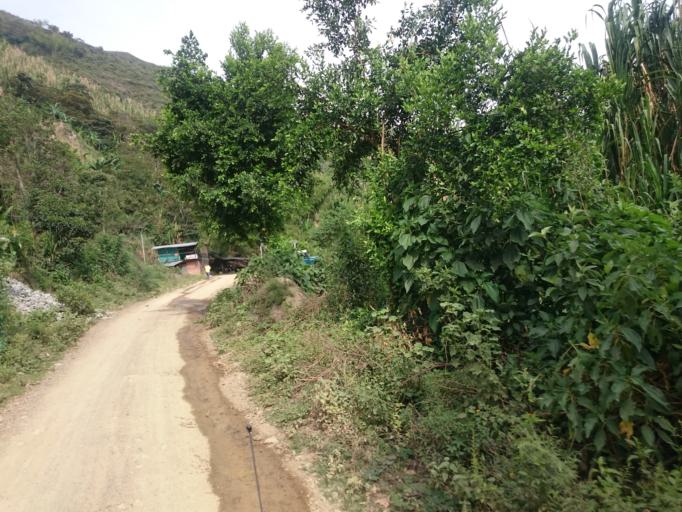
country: CO
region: Cauca
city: Suarez
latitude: 2.9298
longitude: -76.7169
